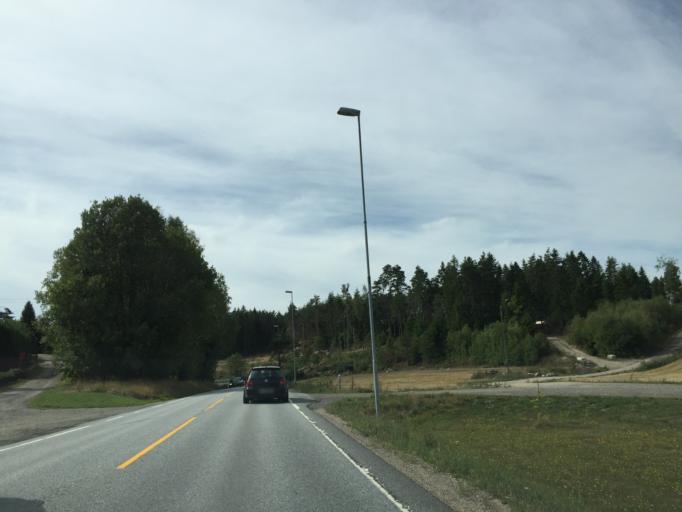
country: NO
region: Ostfold
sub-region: Fredrikstad
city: Fredrikstad
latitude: 59.2747
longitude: 10.8991
